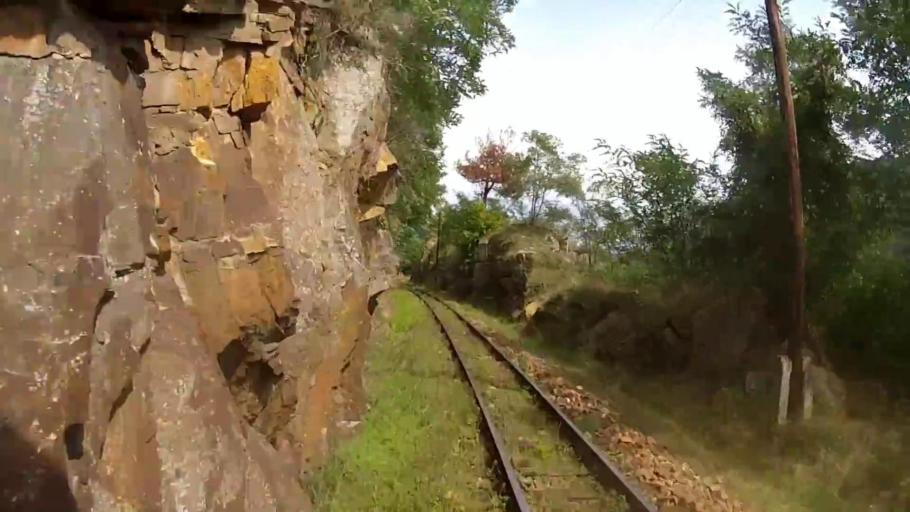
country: BG
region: Blagoevgrad
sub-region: Obshtina Yakoruda
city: Yakoruda
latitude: 42.0294
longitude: 23.6867
